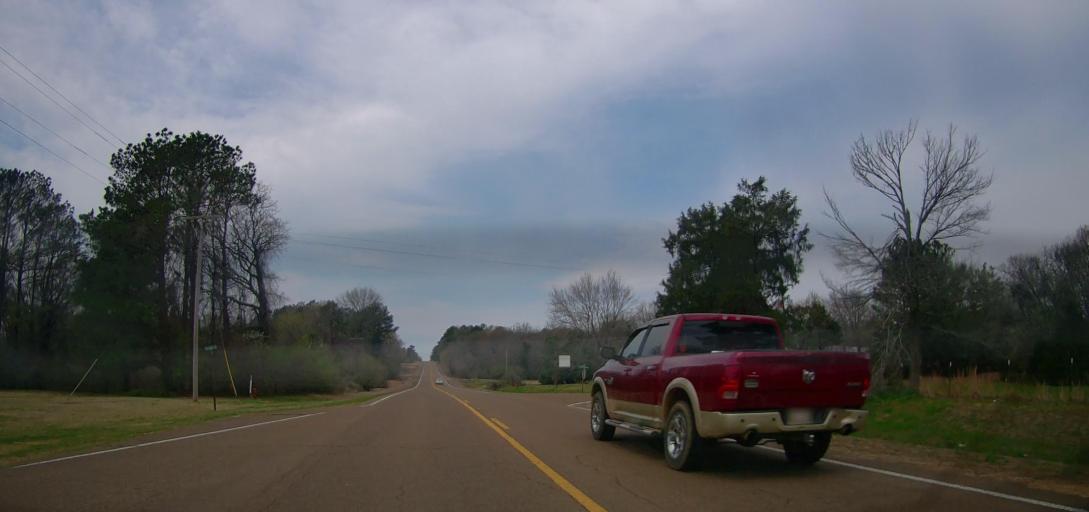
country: US
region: Mississippi
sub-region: Marshall County
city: Byhalia
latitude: 34.8370
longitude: -89.5908
